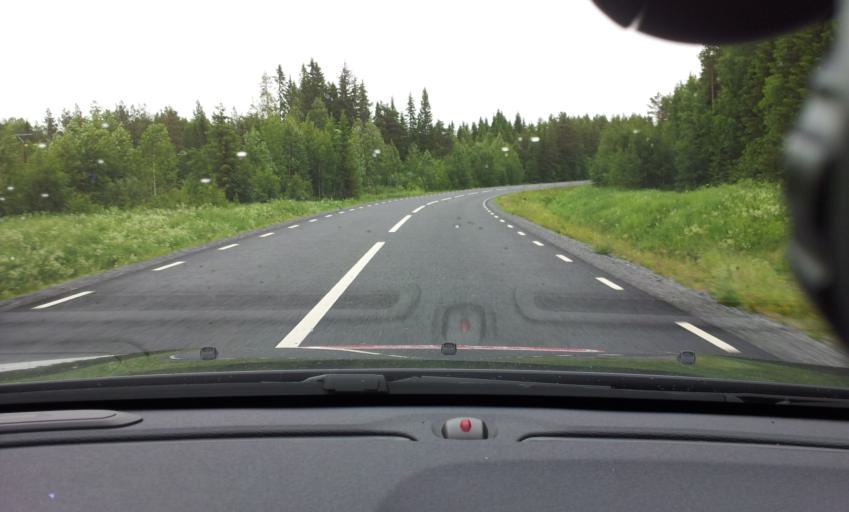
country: SE
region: Jaemtland
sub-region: Stroemsunds Kommun
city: Stroemsund
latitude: 63.6715
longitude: 15.1243
